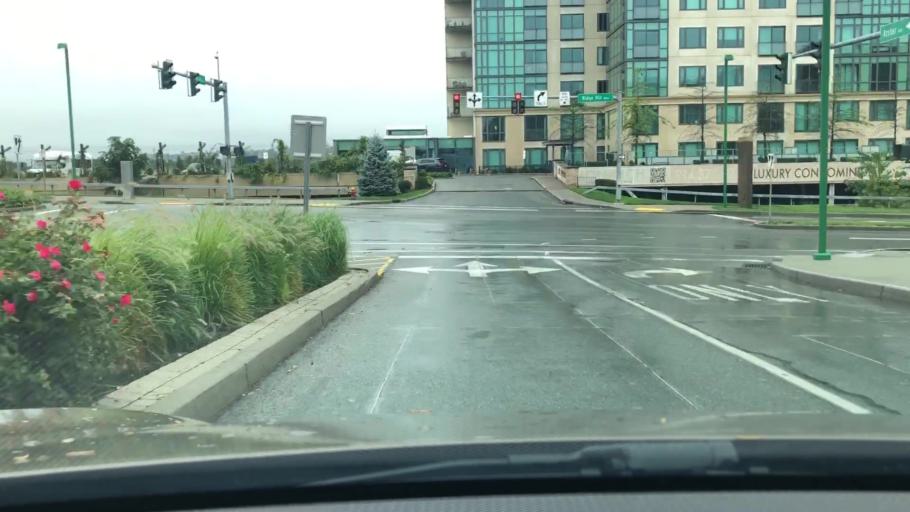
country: US
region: New York
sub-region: Westchester County
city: Tuckahoe
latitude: 40.9634
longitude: -73.8572
